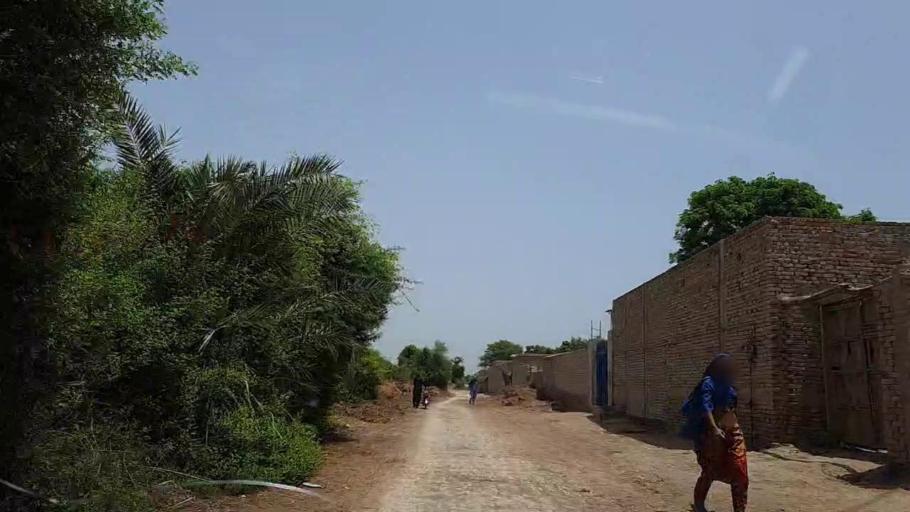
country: PK
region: Sindh
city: Tharu Shah
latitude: 26.9687
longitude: 68.0357
